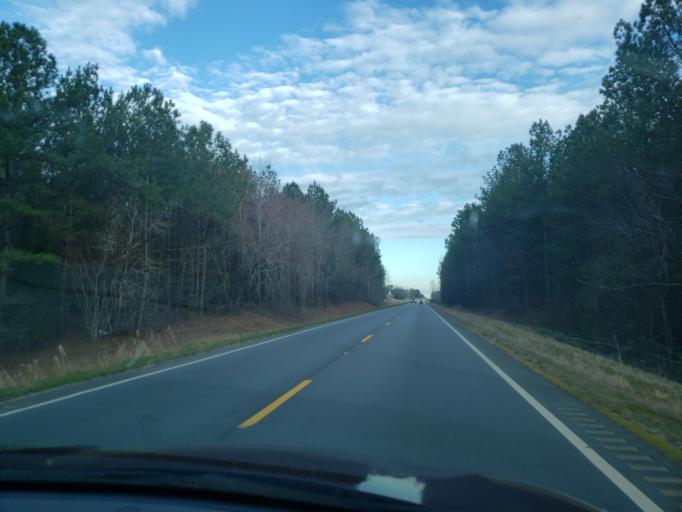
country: US
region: Alabama
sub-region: Randolph County
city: Wedowee
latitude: 33.2691
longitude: -85.4603
